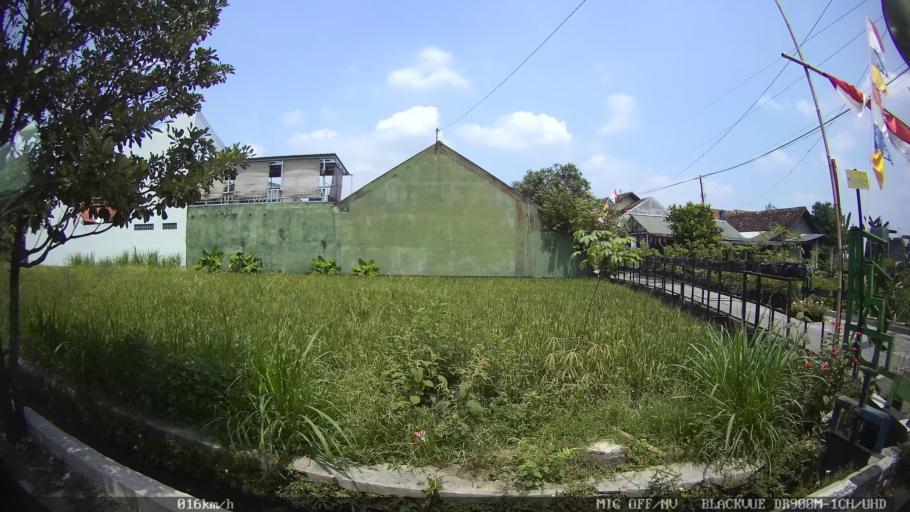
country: ID
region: Daerah Istimewa Yogyakarta
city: Yogyakarta
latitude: -7.8168
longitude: 110.3994
